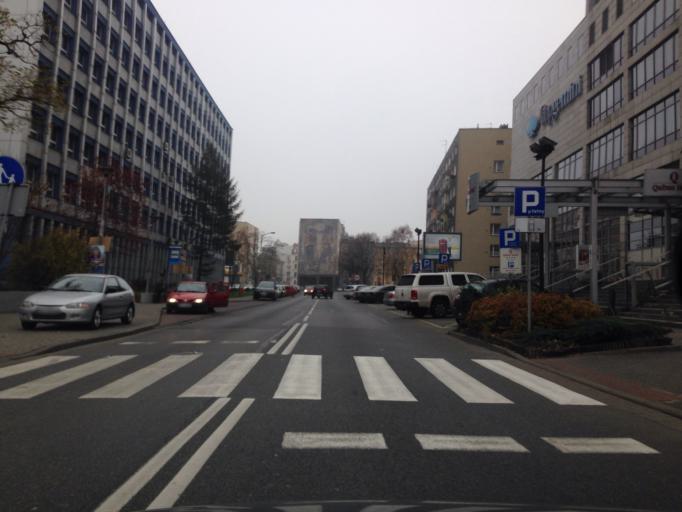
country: PL
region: Silesian Voivodeship
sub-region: Katowice
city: Katowice
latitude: 50.2619
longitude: 19.0257
